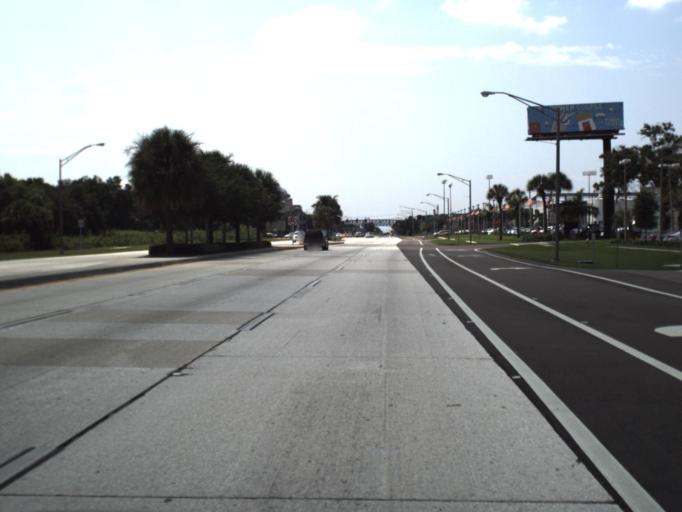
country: US
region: Florida
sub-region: Hillsborough County
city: Egypt Lake-Leto
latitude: 27.9850
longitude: -82.5055
